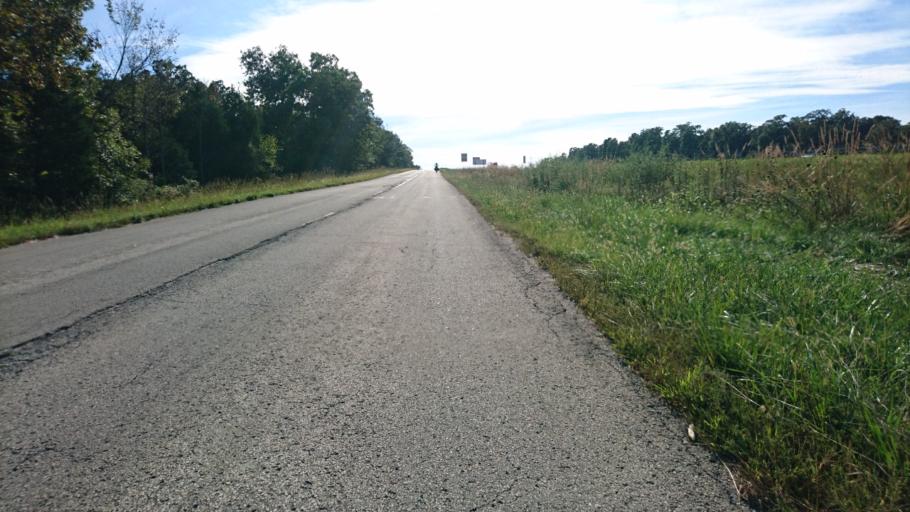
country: US
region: Missouri
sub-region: Crawford County
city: Bourbon
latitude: 38.1168
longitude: -91.3207
